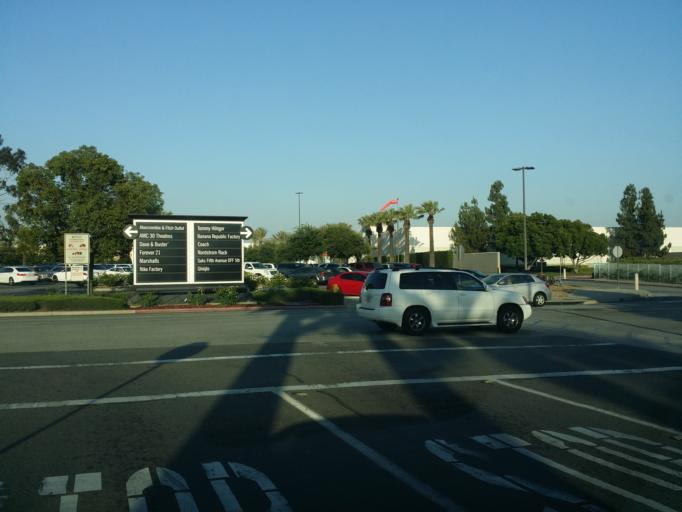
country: US
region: California
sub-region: San Bernardino County
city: Rancho Cucamonga
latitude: 34.0745
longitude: -117.5566
